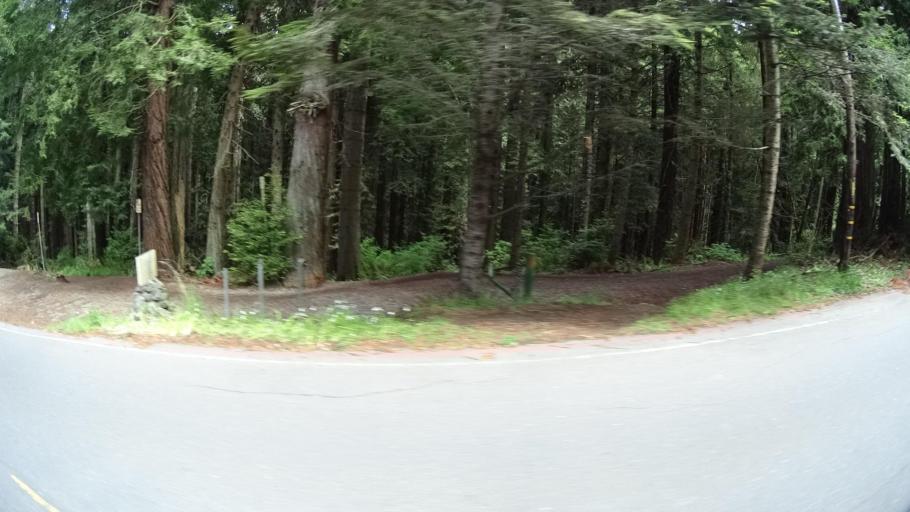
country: US
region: California
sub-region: Humboldt County
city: Arcata
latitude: 40.8687
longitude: -124.0671
